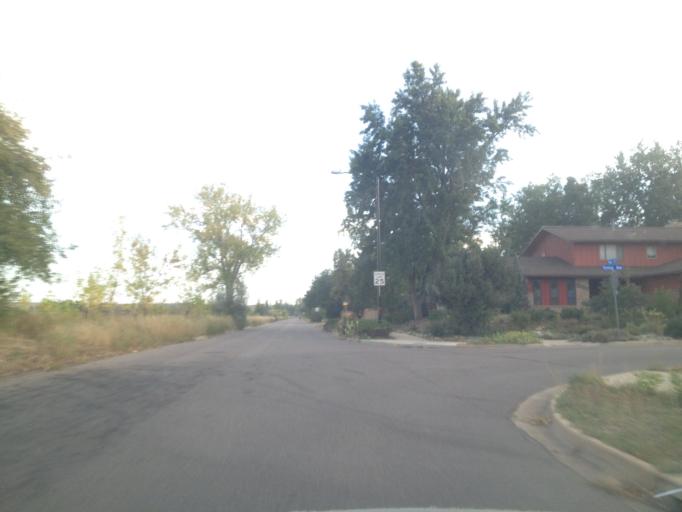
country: US
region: Colorado
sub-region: Boulder County
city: Boulder
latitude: 39.9968
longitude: -105.2244
